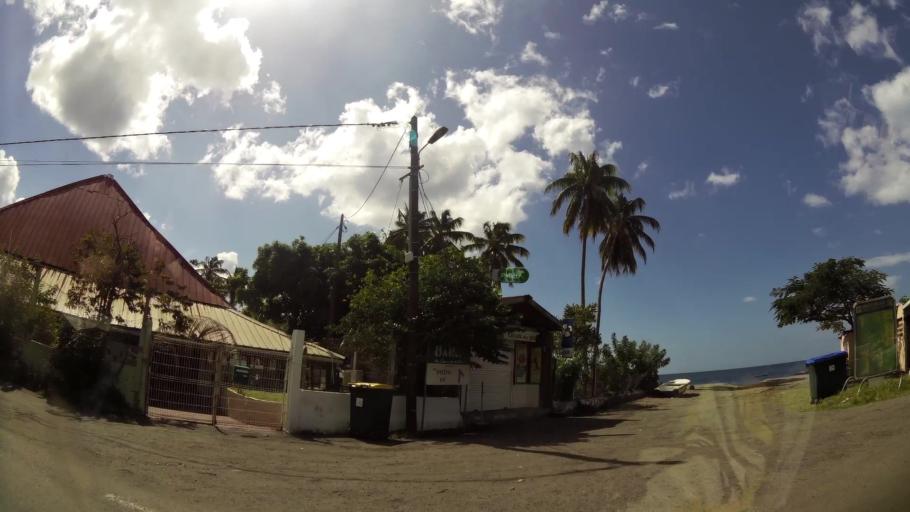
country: MQ
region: Martinique
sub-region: Martinique
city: Saint-Pierre
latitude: 14.7112
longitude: -61.1841
